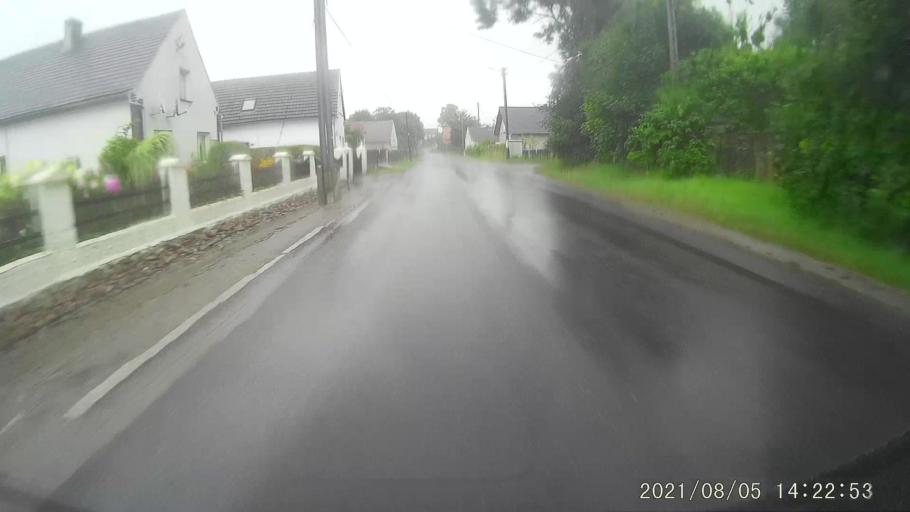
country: PL
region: Opole Voivodeship
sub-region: Powiat nyski
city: Korfantow
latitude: 50.4792
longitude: 17.6523
